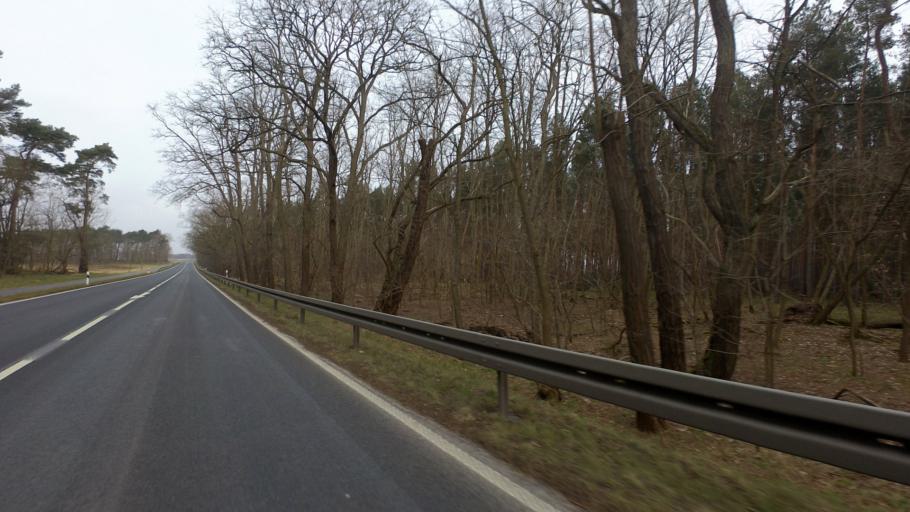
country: DE
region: Brandenburg
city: Beelitz
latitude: 52.2240
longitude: 13.0405
